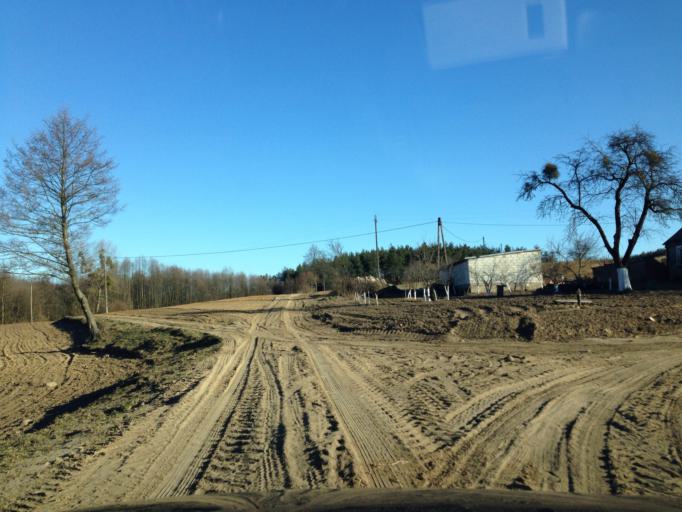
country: PL
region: Kujawsko-Pomorskie
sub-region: Powiat brodnicki
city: Brzozie
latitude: 53.3077
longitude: 19.6561
